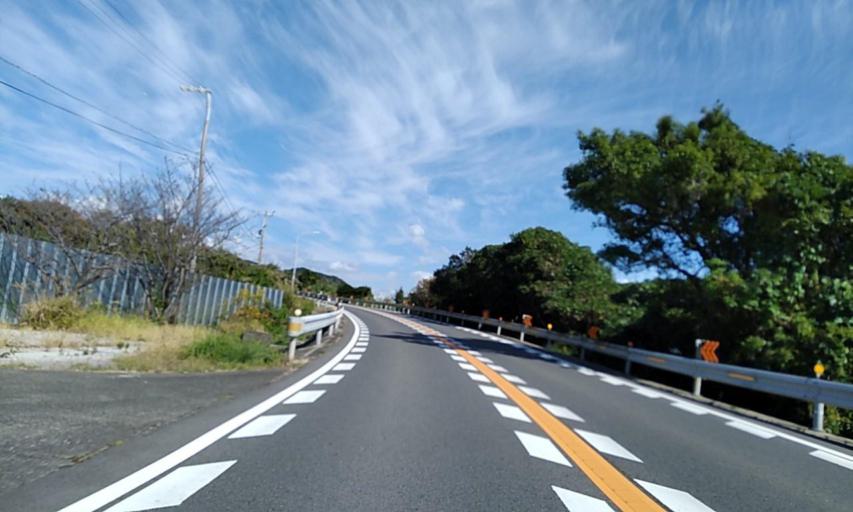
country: JP
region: Wakayama
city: Tanabe
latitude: 33.7808
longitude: 135.2451
